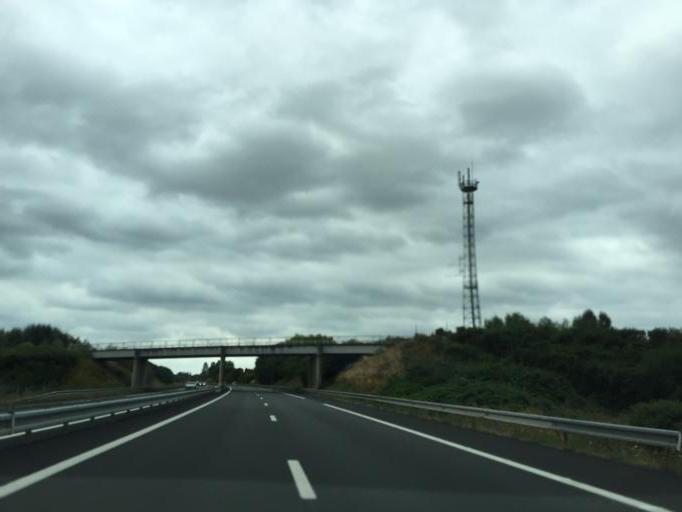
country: FR
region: Pays de la Loire
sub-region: Departement de la Sarthe
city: Brette-les-Pins
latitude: 47.9182
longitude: 0.3000
